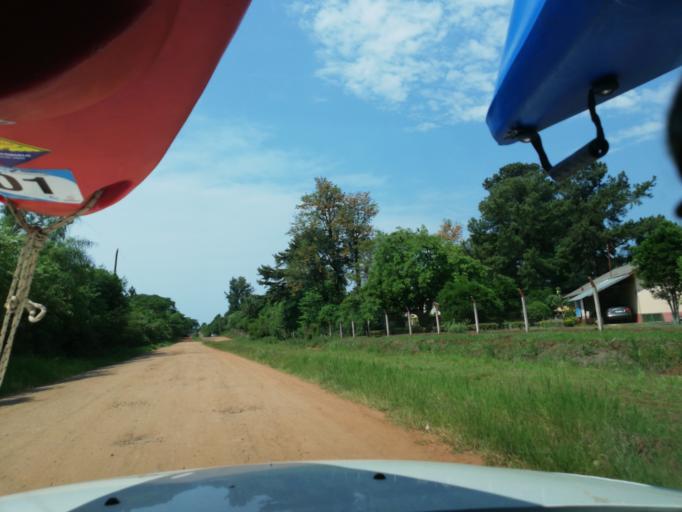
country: AR
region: Misiones
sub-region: Departamento de San Ignacio
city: San Ignacio
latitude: -27.2631
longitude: -55.5488
